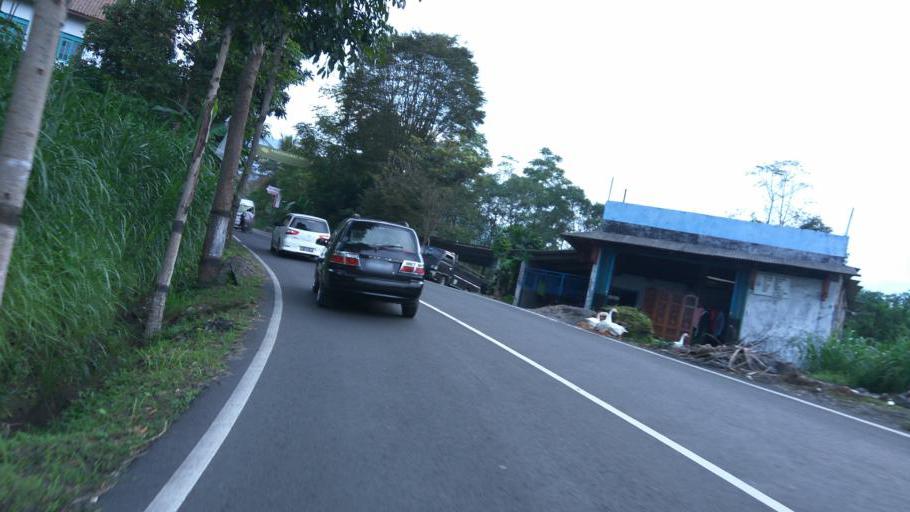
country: ID
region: Central Java
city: Gunung Kendil
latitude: -7.3737
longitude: 110.4426
